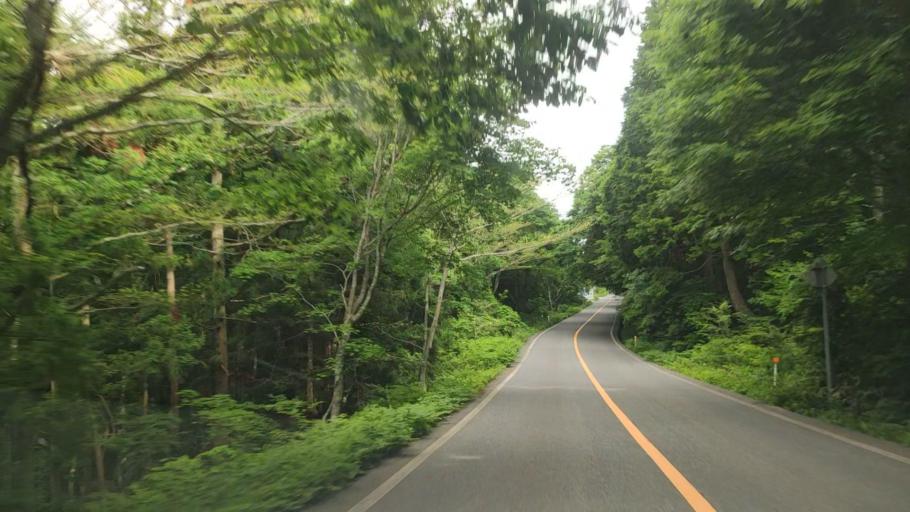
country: JP
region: Tottori
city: Yonago
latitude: 35.3590
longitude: 133.5284
